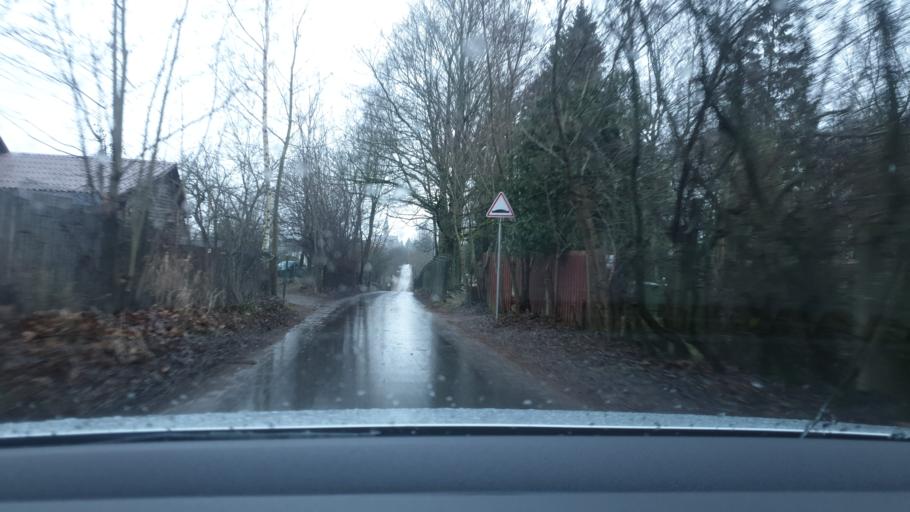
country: LT
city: Skaidiskes
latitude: 54.7046
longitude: 25.4089
